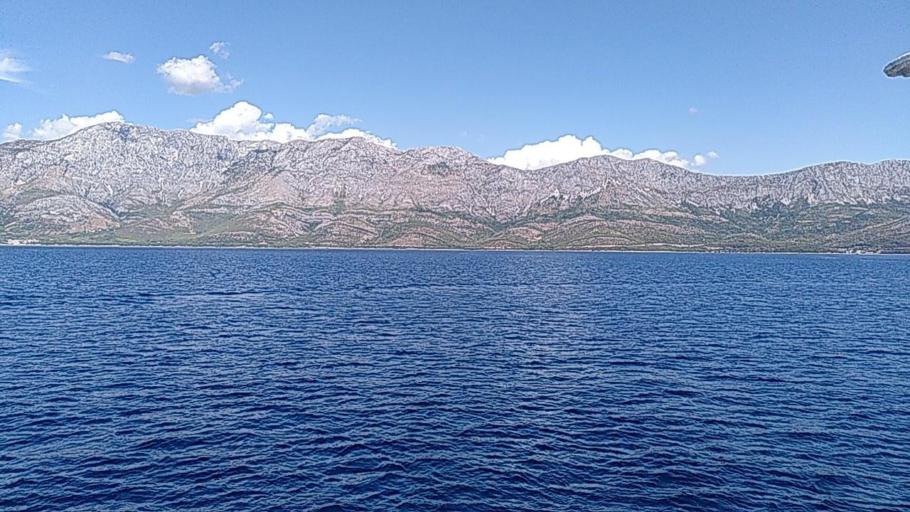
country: HR
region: Dubrovacko-Neretvanska
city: Orebic
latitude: 43.1276
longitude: 17.2049
